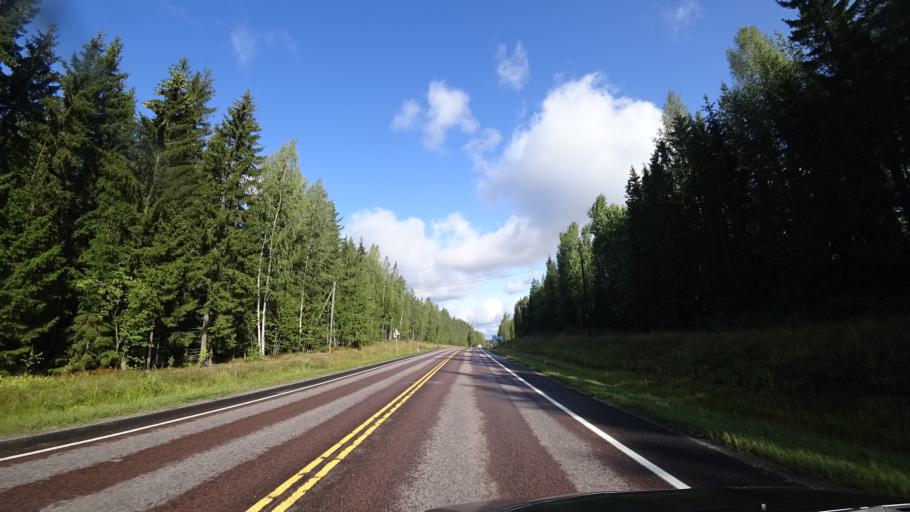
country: FI
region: Uusimaa
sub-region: Helsinki
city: Nurmijaervi
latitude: 60.5067
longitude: 24.9300
